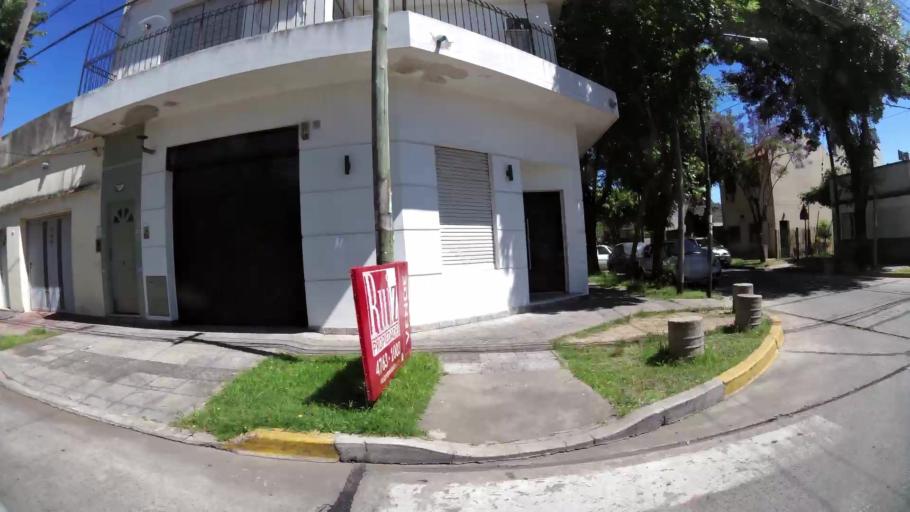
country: AR
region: Buenos Aires
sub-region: Partido de General San Martin
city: General San Martin
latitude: -34.5288
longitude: -58.5542
